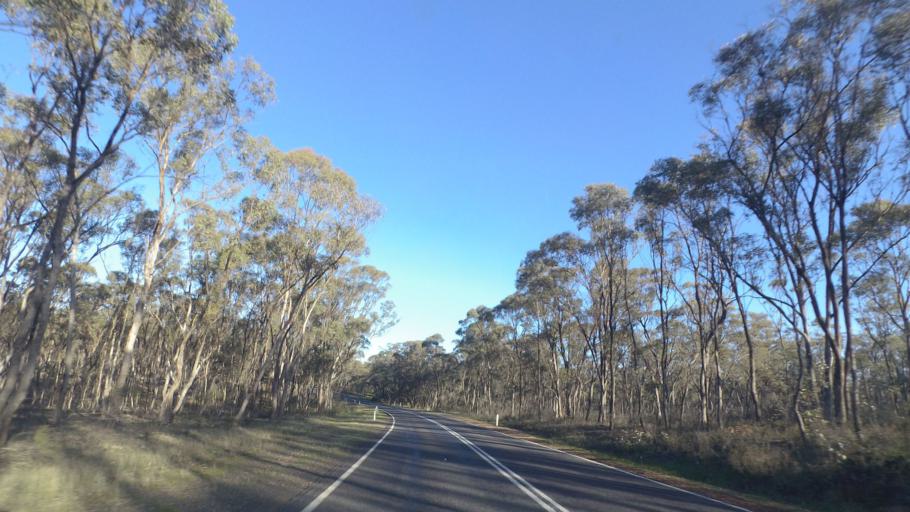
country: AU
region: Victoria
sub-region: Greater Bendigo
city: Kennington
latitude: -36.8903
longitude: 144.4932
